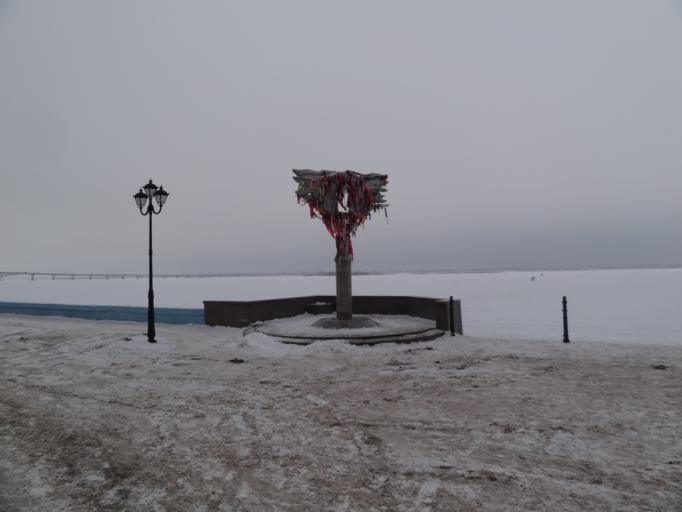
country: RU
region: Saratov
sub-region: Saratovskiy Rayon
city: Saratov
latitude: 51.5229
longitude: 46.0399
